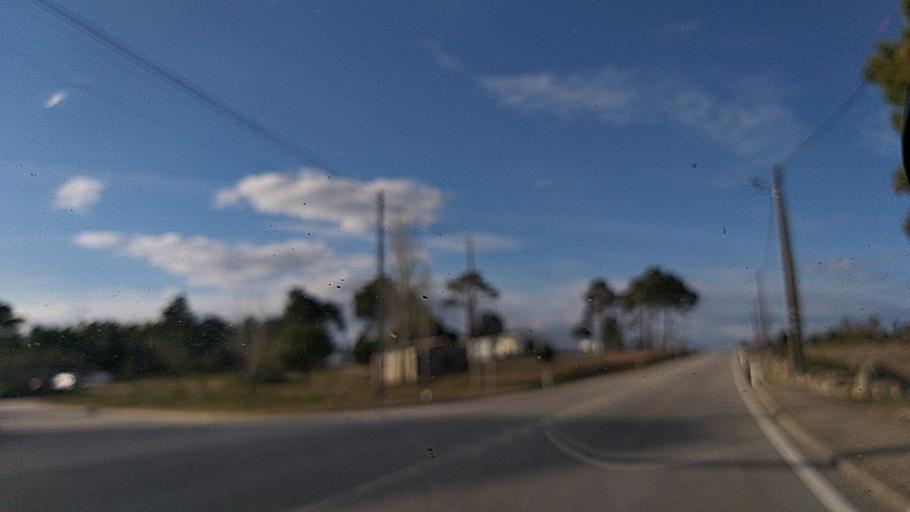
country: ES
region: Castille and Leon
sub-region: Provincia de Salamanca
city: Fuentes de Onoro
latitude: 40.6216
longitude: -6.8461
